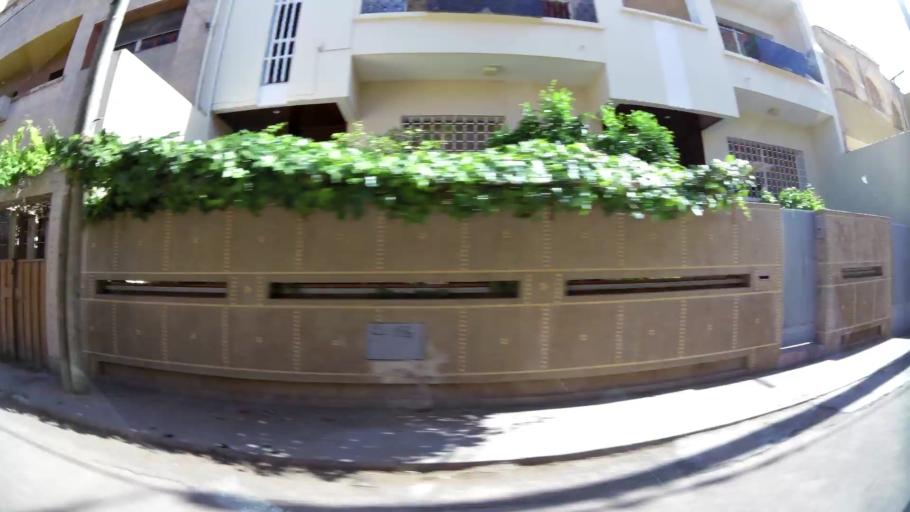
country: MA
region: Oriental
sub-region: Oujda-Angad
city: Oujda
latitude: 34.6669
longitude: -1.9110
